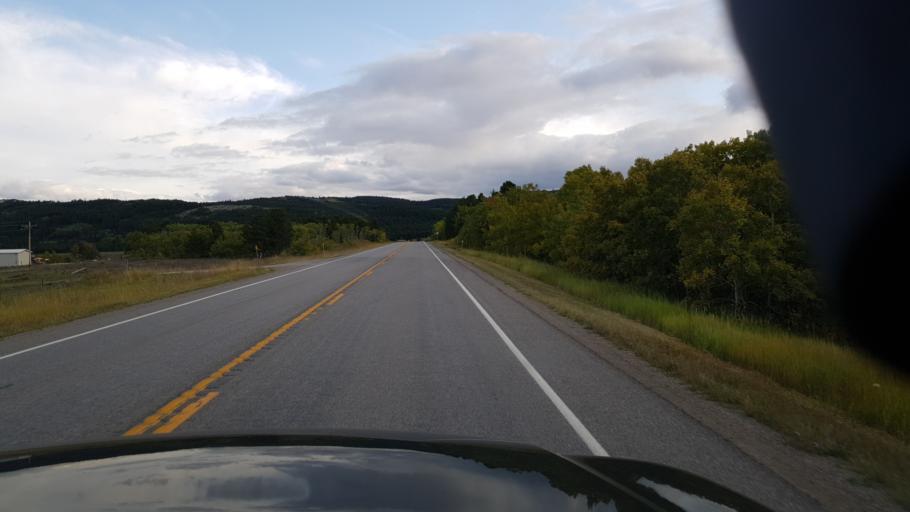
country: US
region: Montana
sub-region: Glacier County
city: South Browning
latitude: 48.4320
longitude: -113.2124
